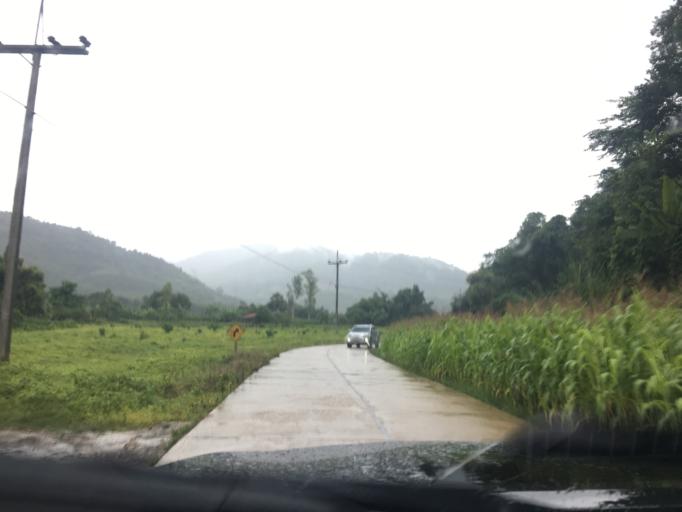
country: TH
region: Chiang Rai
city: Chiang Khong
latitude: 20.2979
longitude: 100.2568
